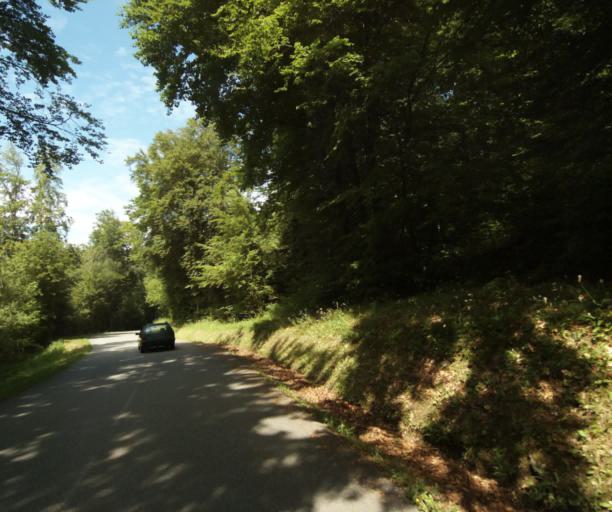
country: FR
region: Rhone-Alpes
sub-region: Departement de la Haute-Savoie
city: Perrignier
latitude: 46.3000
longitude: 6.4679
